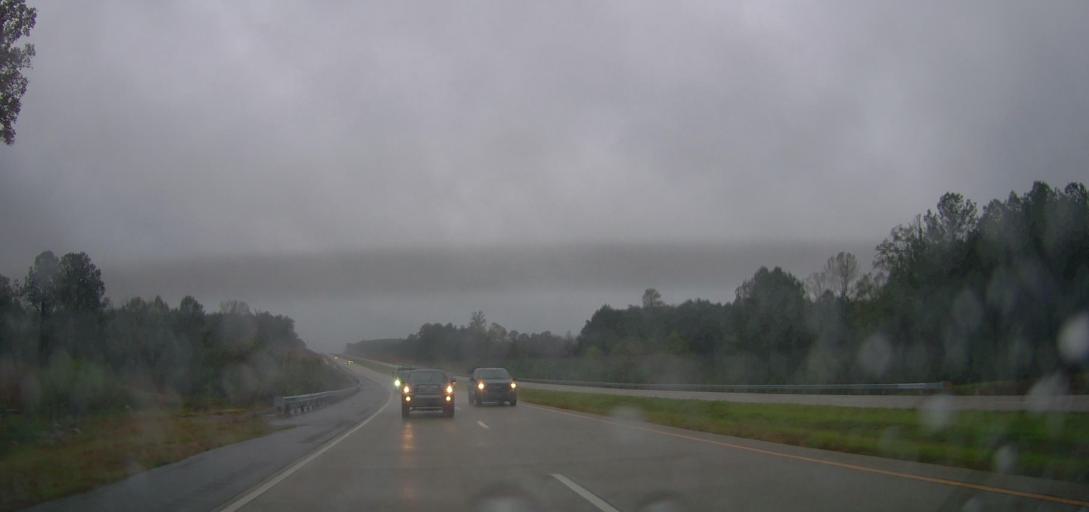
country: US
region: Georgia
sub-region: Jones County
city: Gray
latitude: 33.0087
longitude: -83.5732
